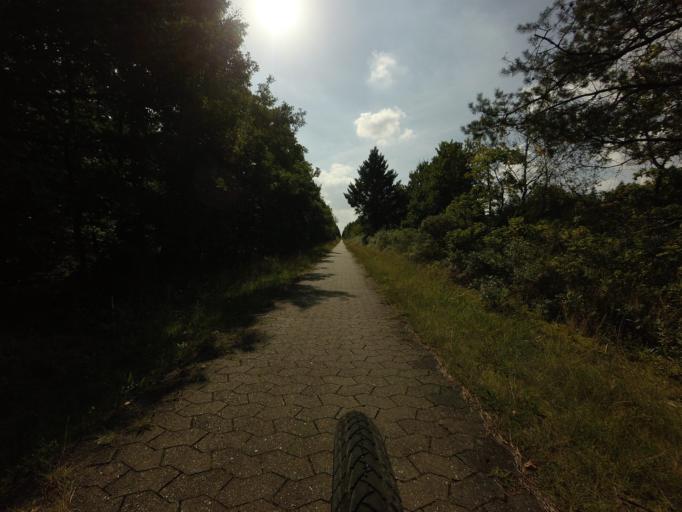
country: DK
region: Central Jutland
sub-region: Viborg Kommune
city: Karup
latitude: 56.2735
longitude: 9.1186
